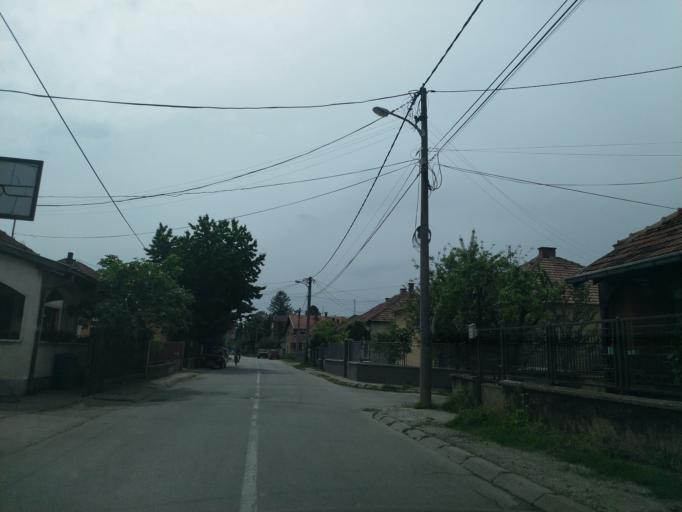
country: RS
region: Central Serbia
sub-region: Pomoravski Okrug
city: Paracin
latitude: 43.8582
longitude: 21.4193
